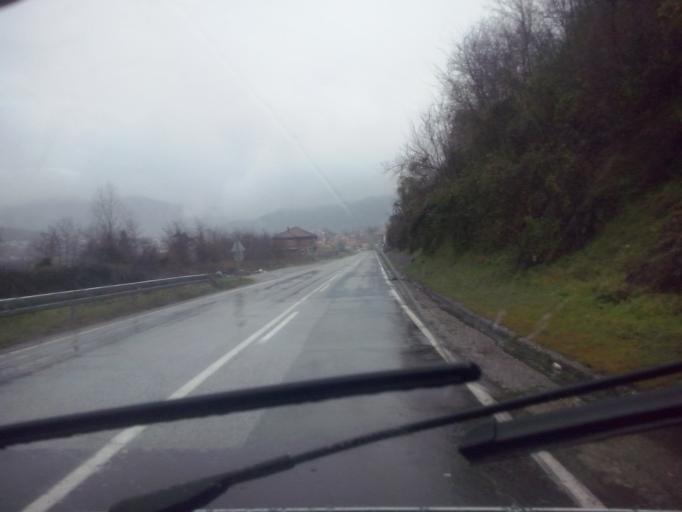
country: RS
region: Central Serbia
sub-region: Raski Okrug
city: Raska
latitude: 43.2737
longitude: 20.6051
